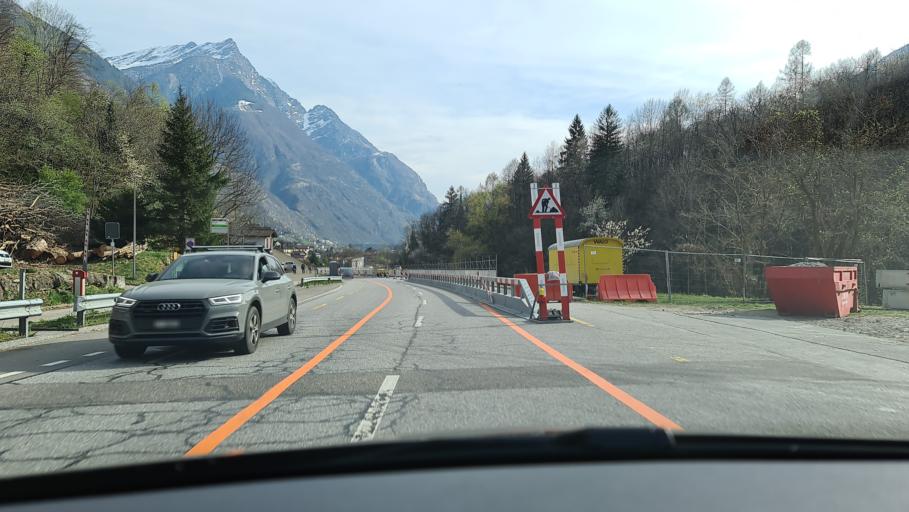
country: CH
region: Ticino
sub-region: Blenio District
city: Malvaglia
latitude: 46.4207
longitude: 8.9771
